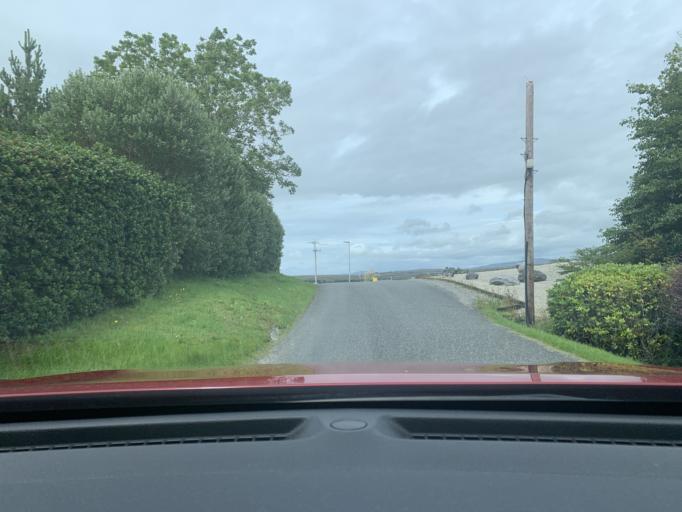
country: IE
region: Ulster
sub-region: County Donegal
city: Dungloe
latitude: 54.9432
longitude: -8.3584
